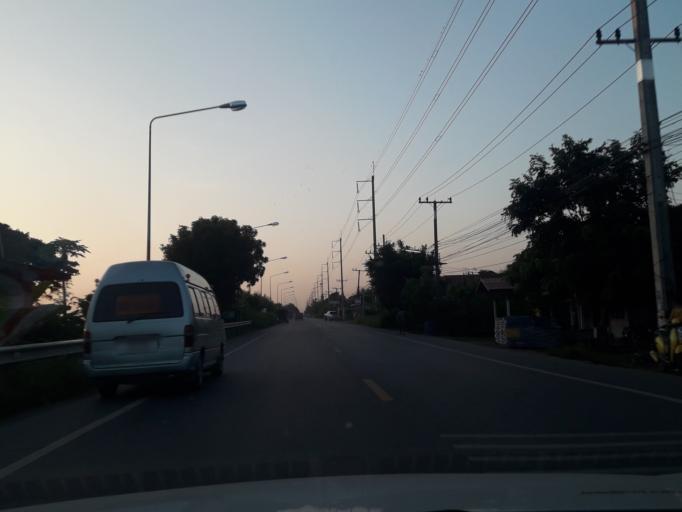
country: TH
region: Phra Nakhon Si Ayutthaya
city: Maha Rat
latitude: 14.5149
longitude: 100.5450
